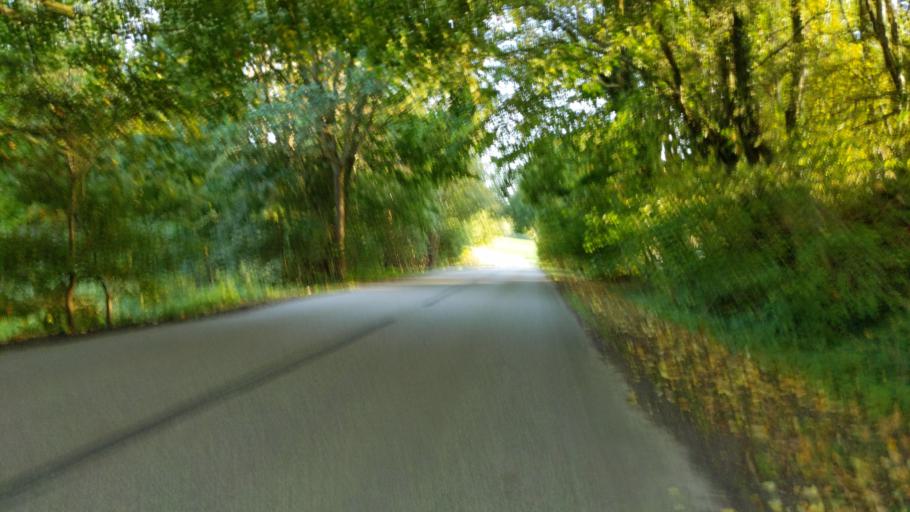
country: DE
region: Schleswig-Holstein
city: Susel
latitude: 54.0629
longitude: 10.7212
